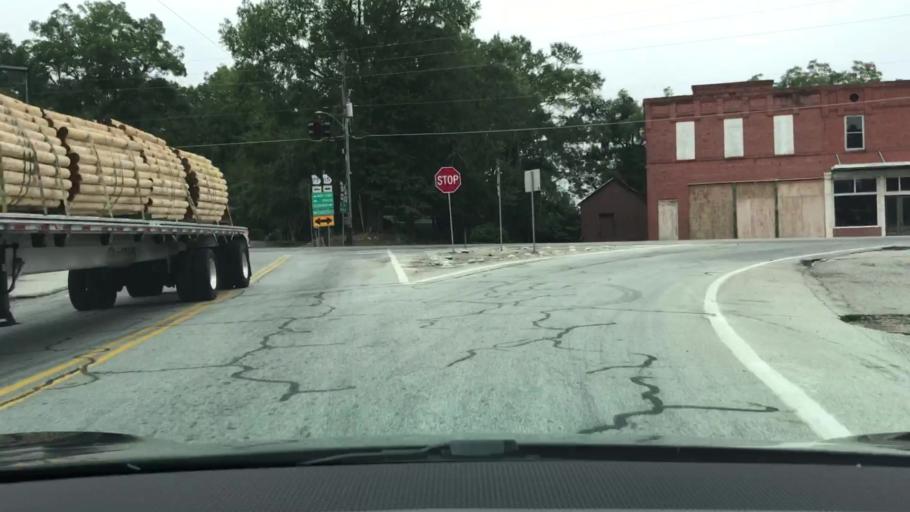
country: US
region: Georgia
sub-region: Greene County
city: Union Point
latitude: 33.5368
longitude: -83.0811
